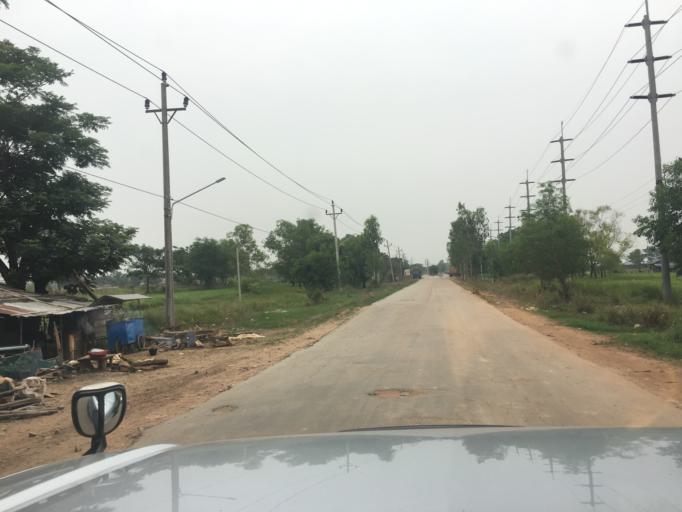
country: MM
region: Yangon
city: Syriam
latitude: 16.9486
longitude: 96.2792
